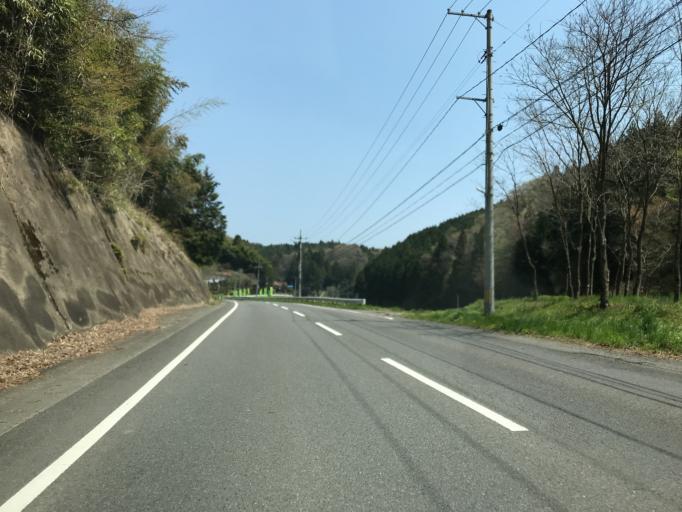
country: JP
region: Fukushima
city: Ishikawa
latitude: 37.0661
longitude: 140.4386
